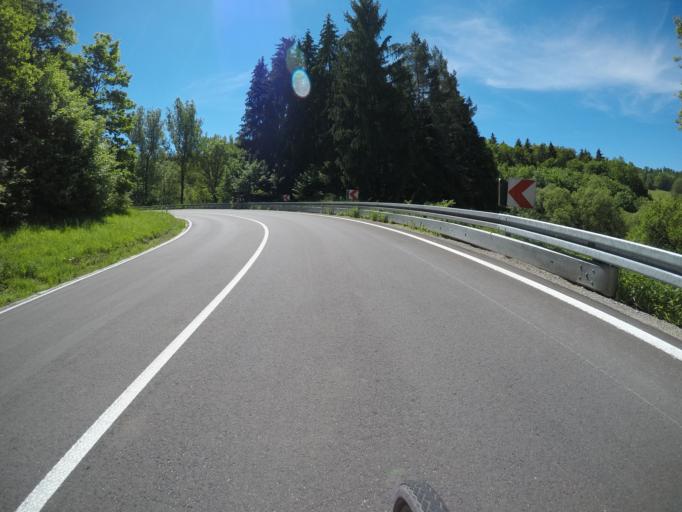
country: DE
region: Baden-Wuerttemberg
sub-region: Karlsruhe Region
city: Neuhausen
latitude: 48.8080
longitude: 8.8051
